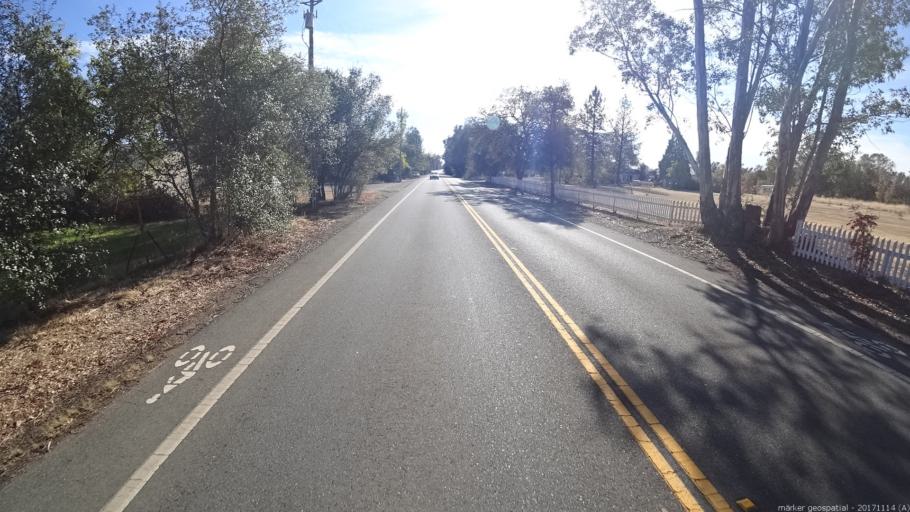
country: US
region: California
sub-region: Shasta County
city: Anderson
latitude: 40.4422
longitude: -122.4077
